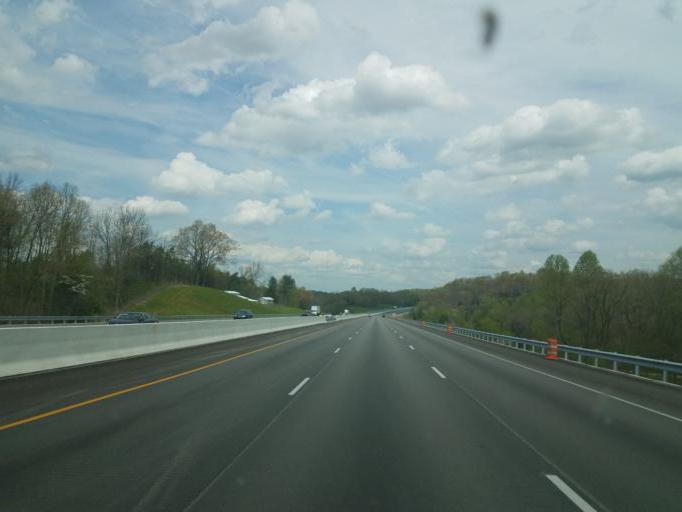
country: US
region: Kentucky
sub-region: Hart County
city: Munfordville
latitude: 37.3297
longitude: -85.9068
